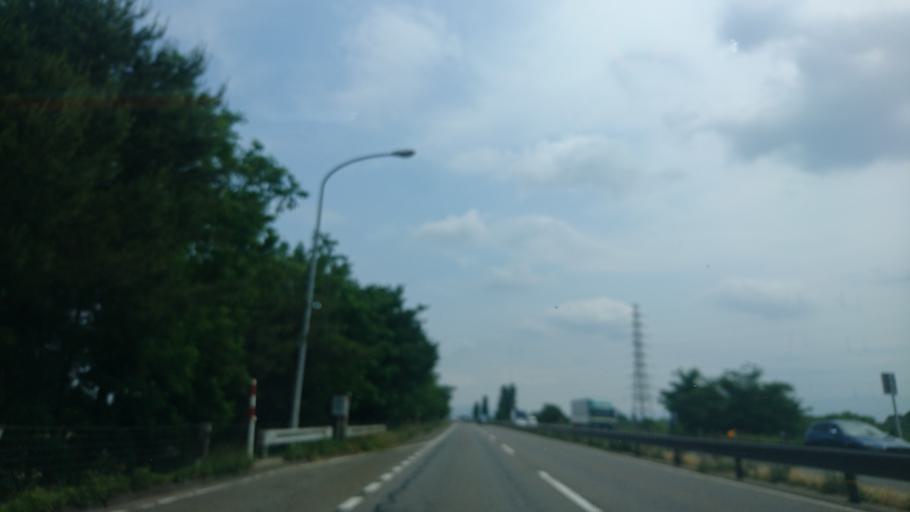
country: JP
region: Niigata
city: Suibara
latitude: 37.9457
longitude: 139.1920
